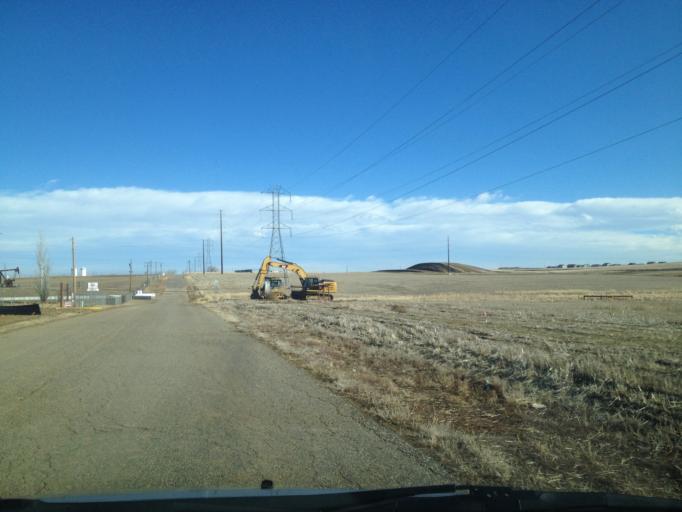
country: US
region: Colorado
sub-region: Weld County
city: Dacono
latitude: 40.0583
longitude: -104.9763
